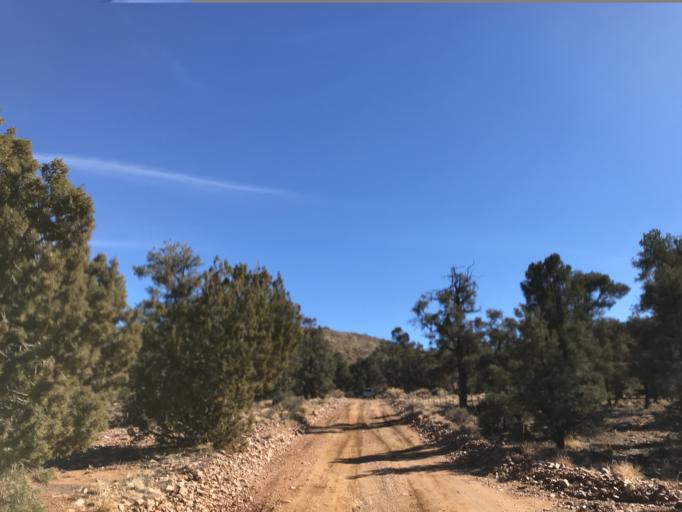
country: US
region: California
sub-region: San Bernardino County
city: Big Bear City
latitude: 34.2553
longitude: -116.7410
